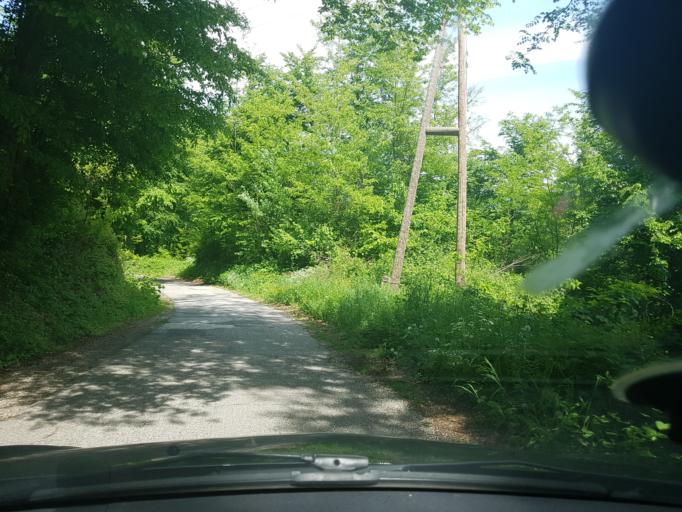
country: SI
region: Rogatec
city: Rogatec
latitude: 46.2103
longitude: 15.7195
